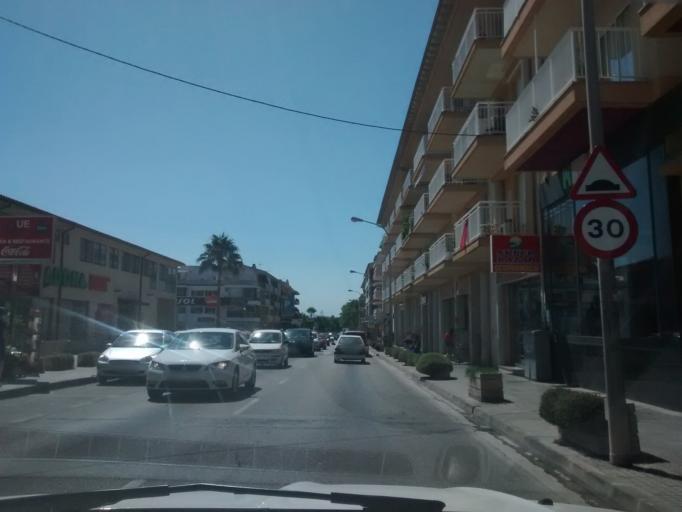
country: ES
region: Balearic Islands
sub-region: Illes Balears
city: Alcudia
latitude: 39.8506
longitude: 3.1265
